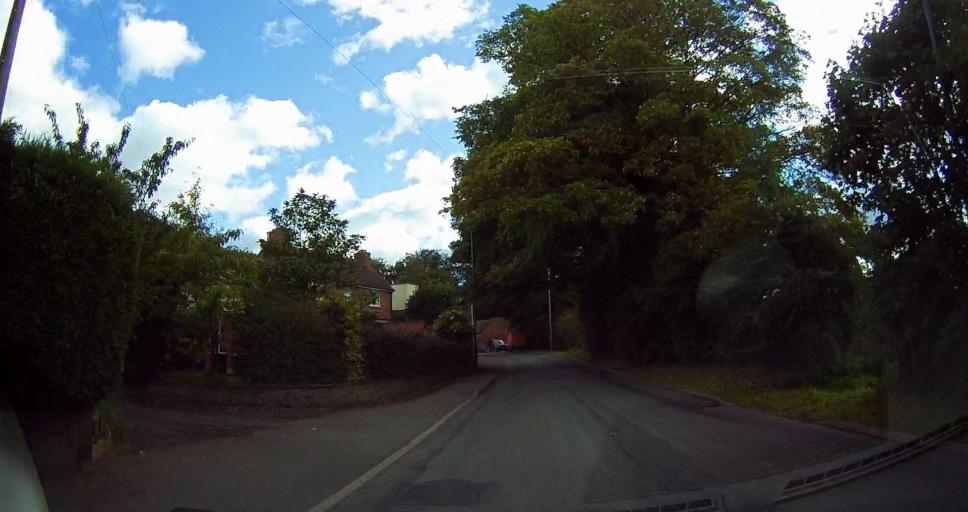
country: GB
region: England
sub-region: Cheshire East
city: Chorlton
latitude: 52.9783
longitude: -2.4056
